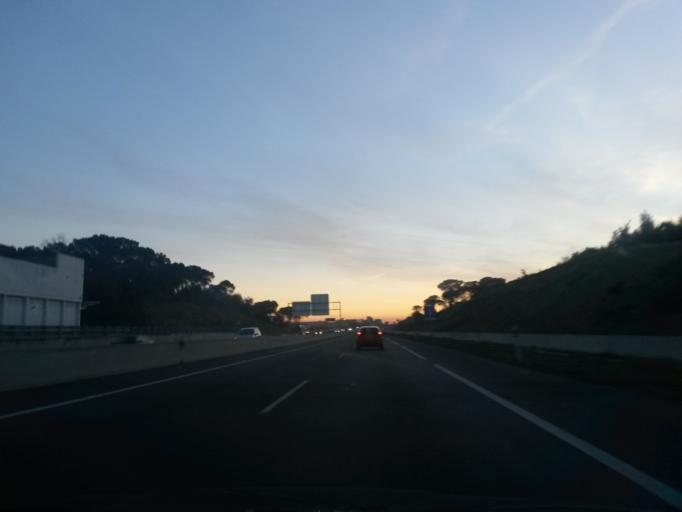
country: ES
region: Catalonia
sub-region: Provincia de Girona
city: Riudellots de la Selva
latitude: 41.9129
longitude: 2.7906
